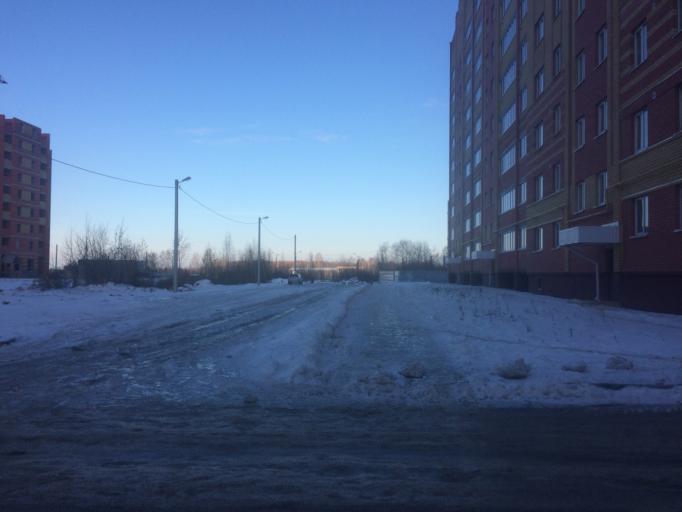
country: RU
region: Mariy-El
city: Yoshkar-Ola
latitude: 56.6411
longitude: 47.9255
